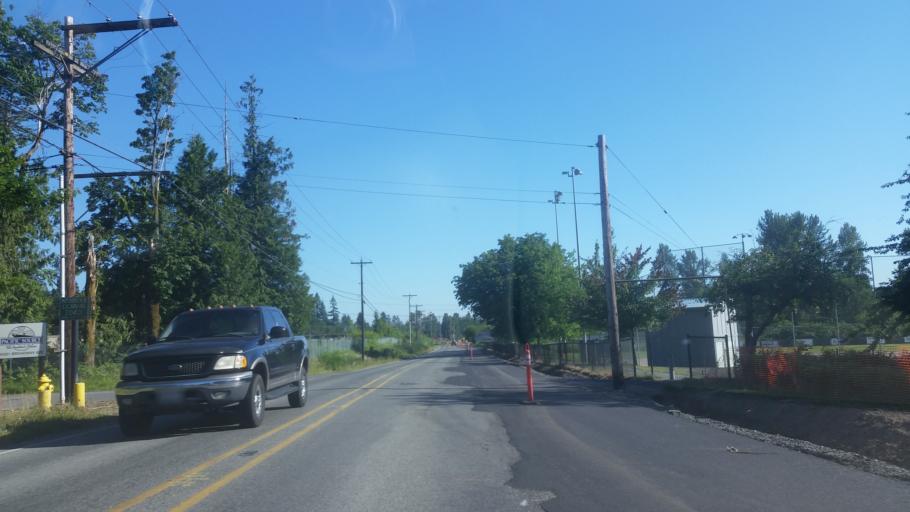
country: US
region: Washington
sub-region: Snohomish County
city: Maltby
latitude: 47.8125
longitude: -122.1101
